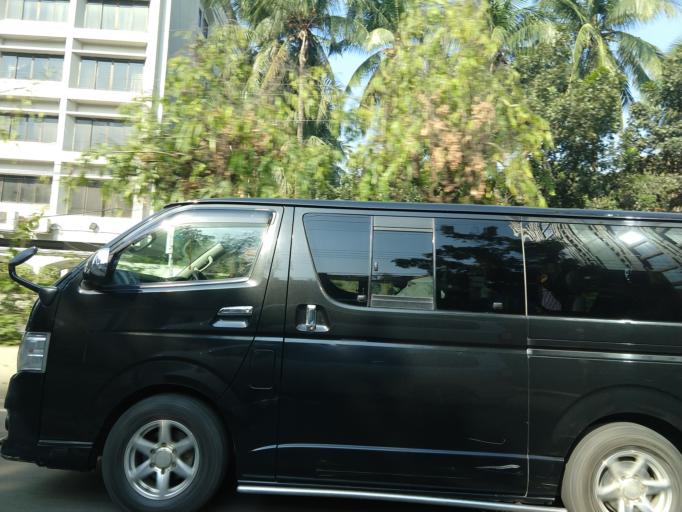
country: BD
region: Dhaka
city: Paltan
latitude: 23.7855
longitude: 90.4170
